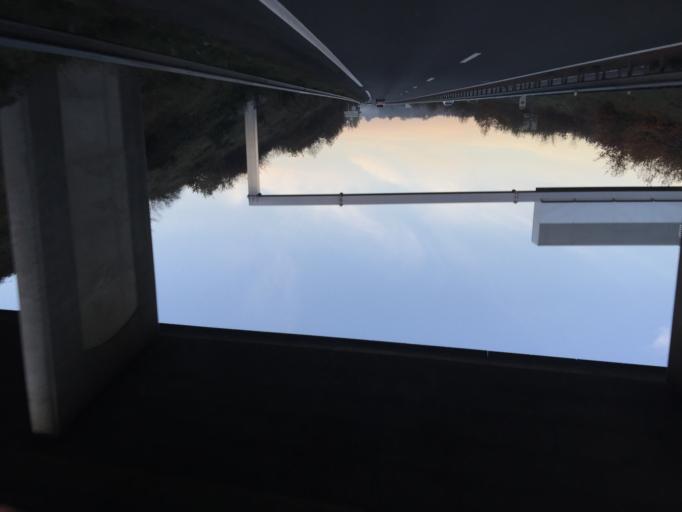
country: FR
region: Rhone-Alpes
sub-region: Departement de la Loire
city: Neulise
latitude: 45.8899
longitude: 4.1746
